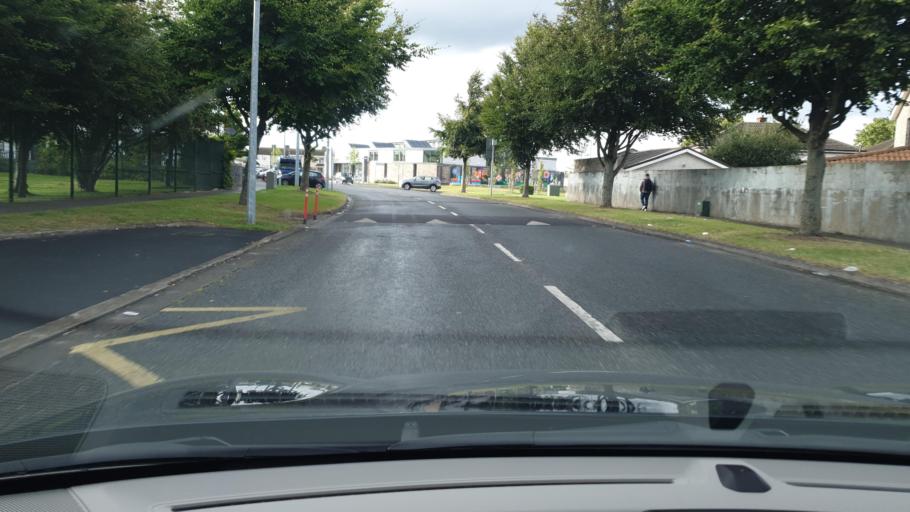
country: IE
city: Palmerstown
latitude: 53.3434
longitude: -6.3943
